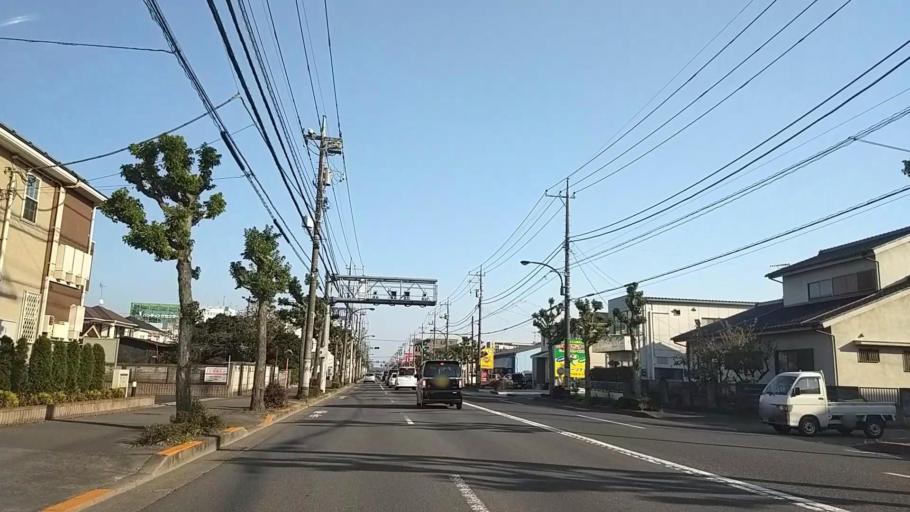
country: JP
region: Tokyo
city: Fussa
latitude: 35.7841
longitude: 139.3140
